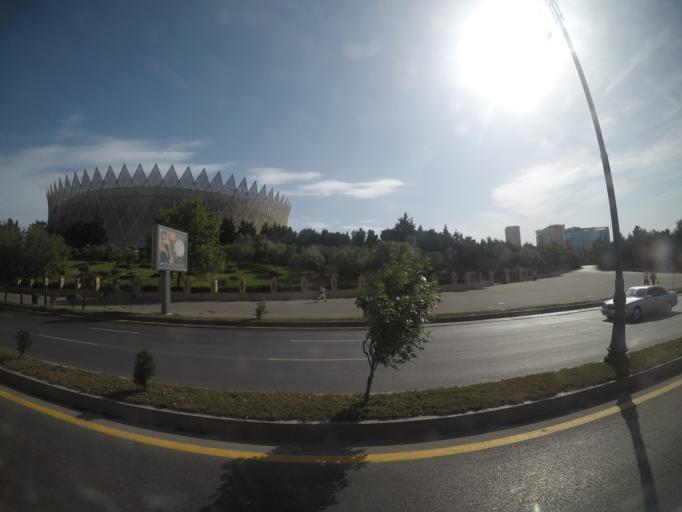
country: AZ
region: Baki
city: Badamdar
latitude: 40.3904
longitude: 49.8244
